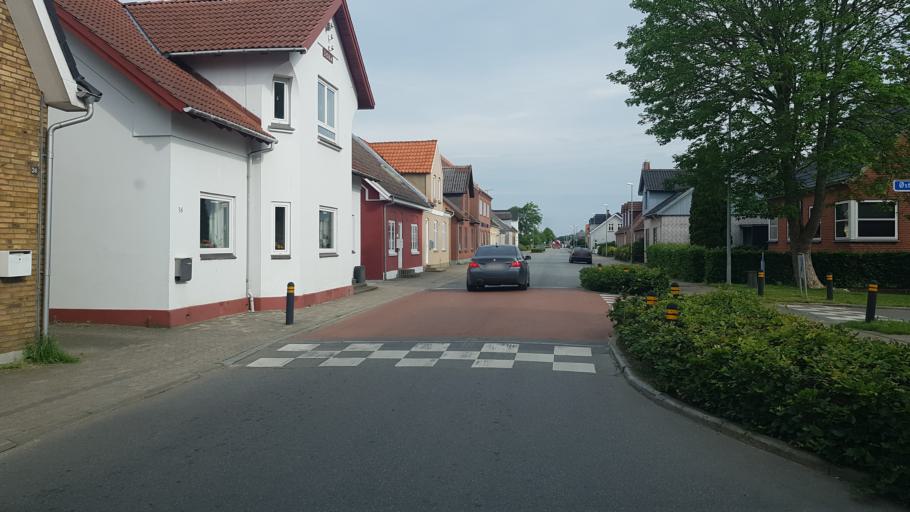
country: DK
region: South Denmark
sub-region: Esbjerg Kommune
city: Bramming
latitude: 55.4715
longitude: 8.8008
